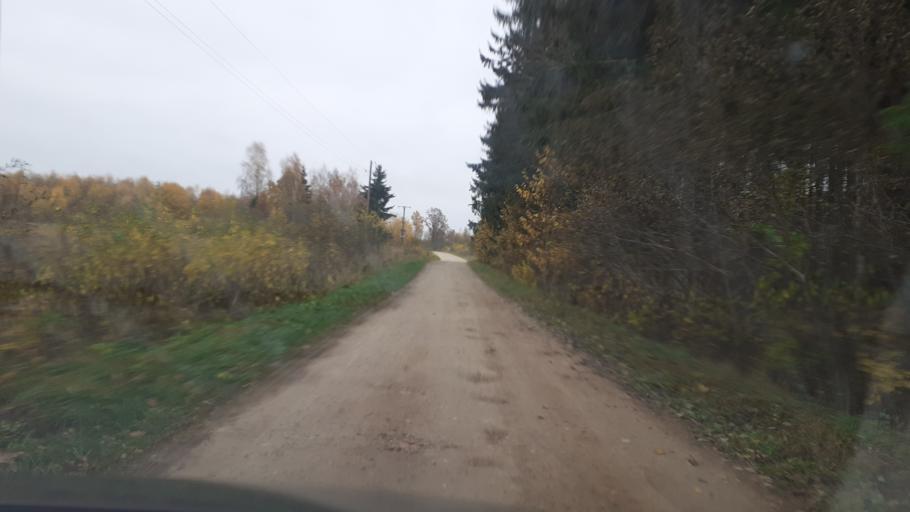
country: LV
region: Saldus Rajons
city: Saldus
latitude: 56.8618
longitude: 22.3315
